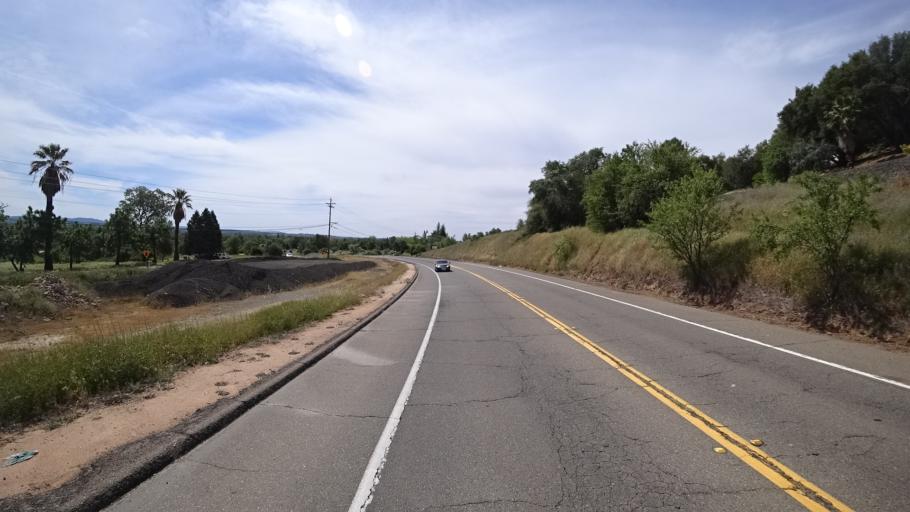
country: US
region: California
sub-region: Placer County
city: Loomis
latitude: 38.8368
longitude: -121.2202
